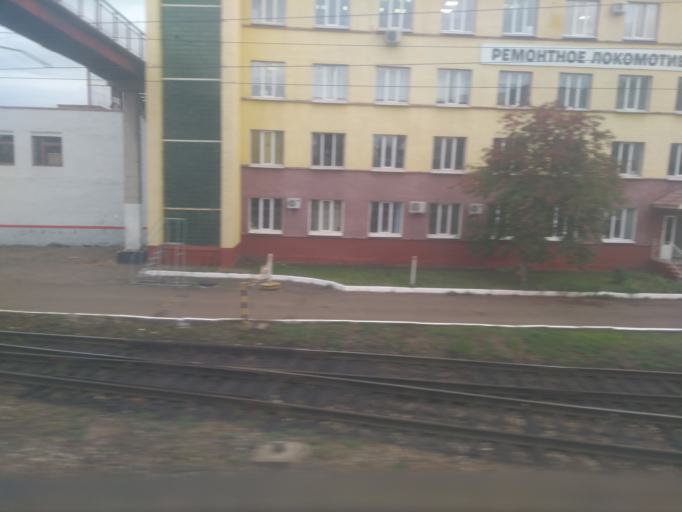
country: RU
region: Tatarstan
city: Osinovo
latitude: 55.8172
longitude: 48.8998
